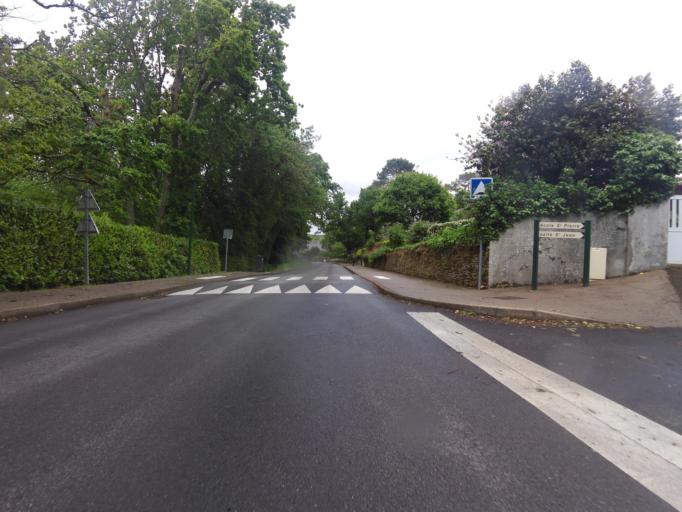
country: FR
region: Brittany
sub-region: Departement du Morbihan
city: Baden
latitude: 47.6197
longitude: -2.9220
